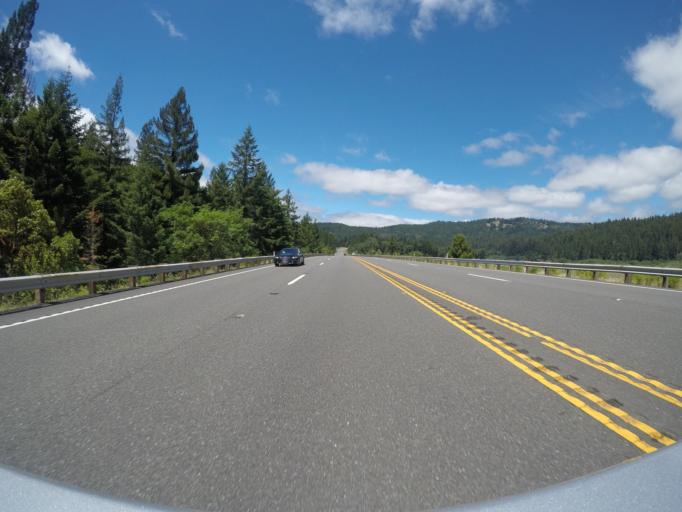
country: US
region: California
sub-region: Humboldt County
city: Redway
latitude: 40.2416
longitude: -123.8322
